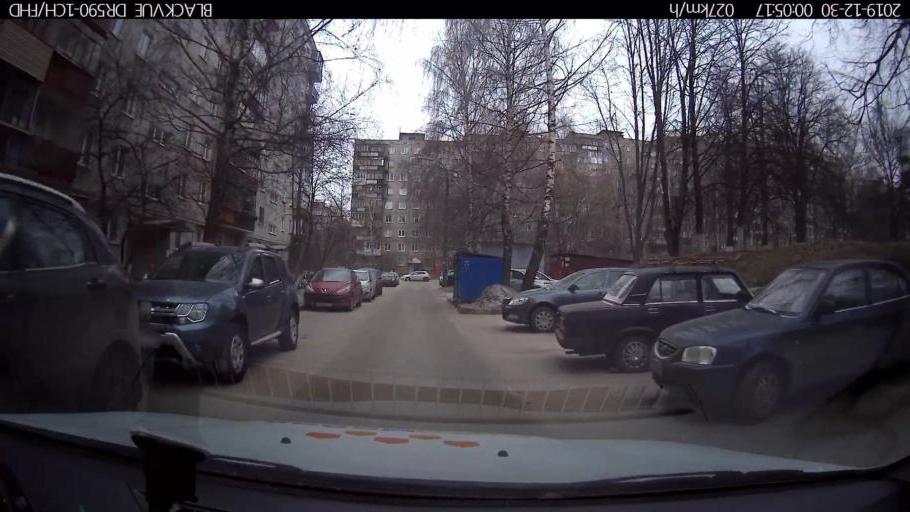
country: RU
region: Nizjnij Novgorod
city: Nizhniy Novgorod
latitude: 56.3144
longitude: 44.0482
